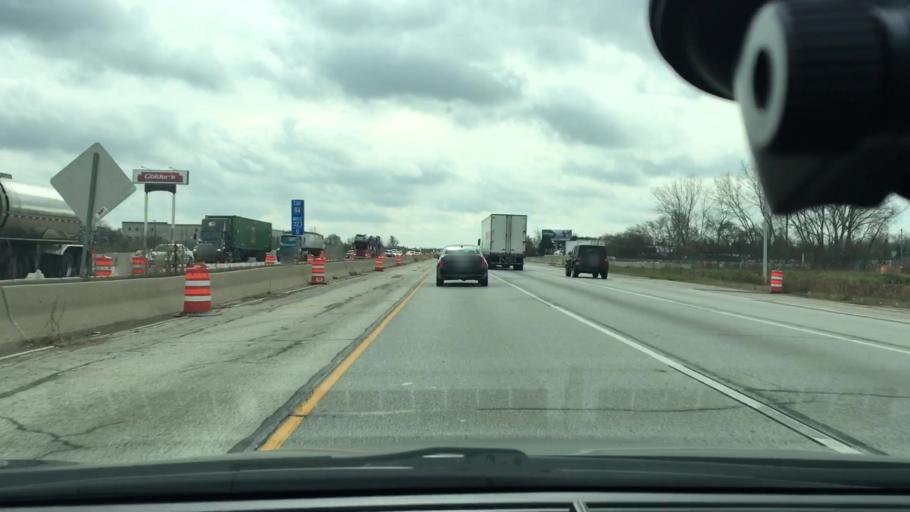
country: US
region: Wisconsin
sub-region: Racine County
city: Caledonia
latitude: 42.8705
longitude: -87.9374
